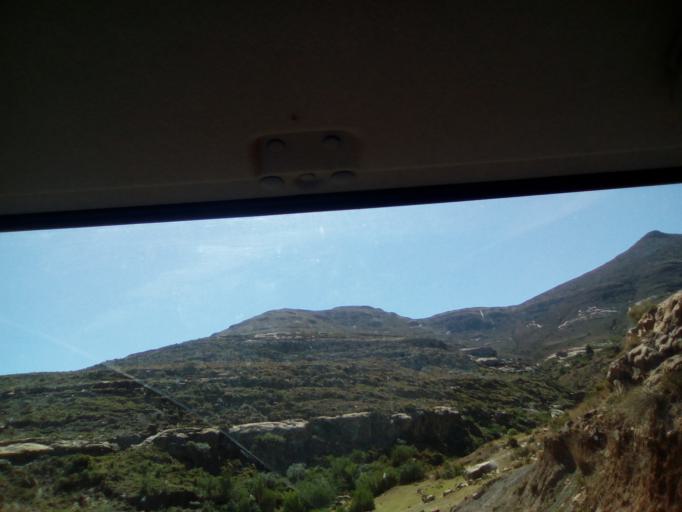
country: LS
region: Qacha's Nek
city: Qacha's Nek
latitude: -30.0420
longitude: 28.6611
